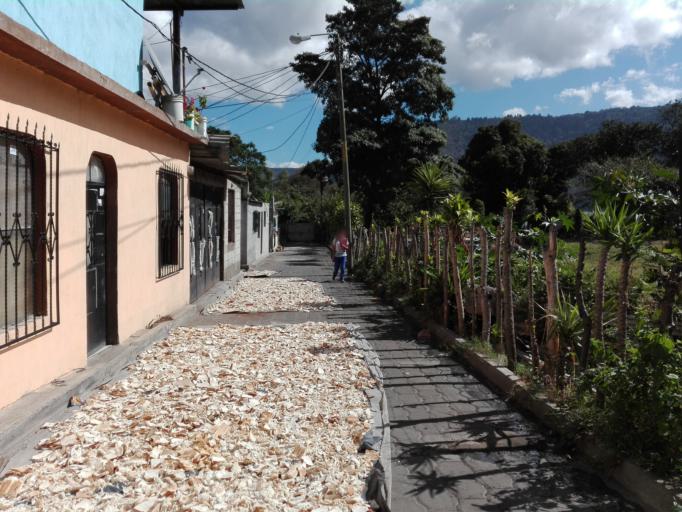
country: GT
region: Guatemala
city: Villa Canales
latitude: 14.4261
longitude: -90.5528
